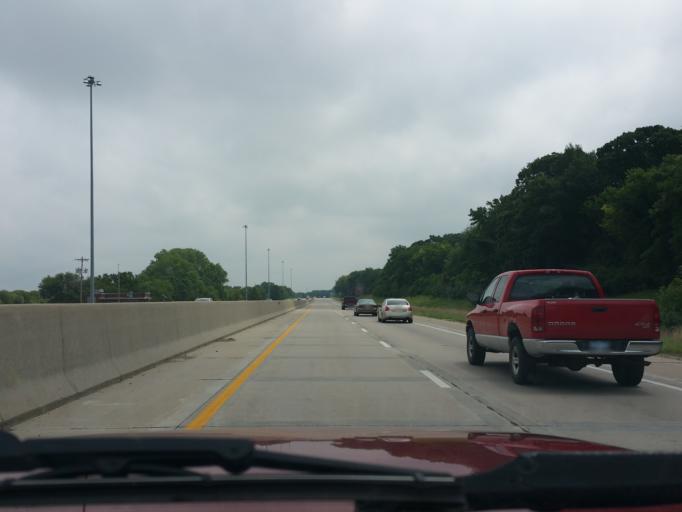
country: US
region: Kansas
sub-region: Shawnee County
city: Topeka
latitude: 39.0668
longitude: -95.6937
